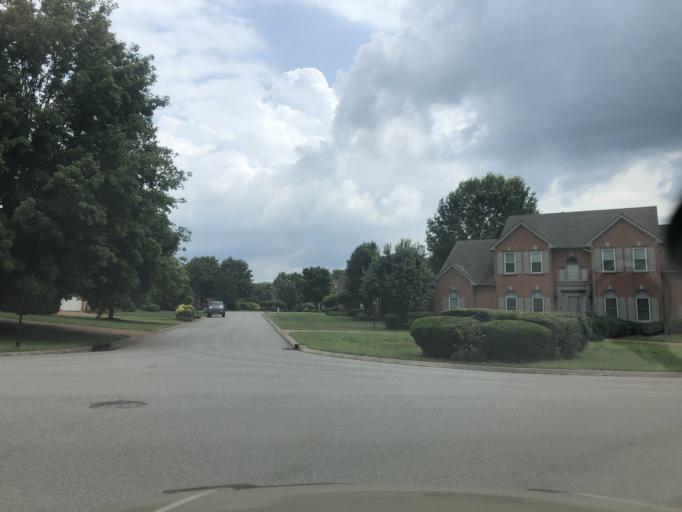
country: US
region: Tennessee
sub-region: Davidson County
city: Lakewood
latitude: 36.2322
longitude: -86.6056
